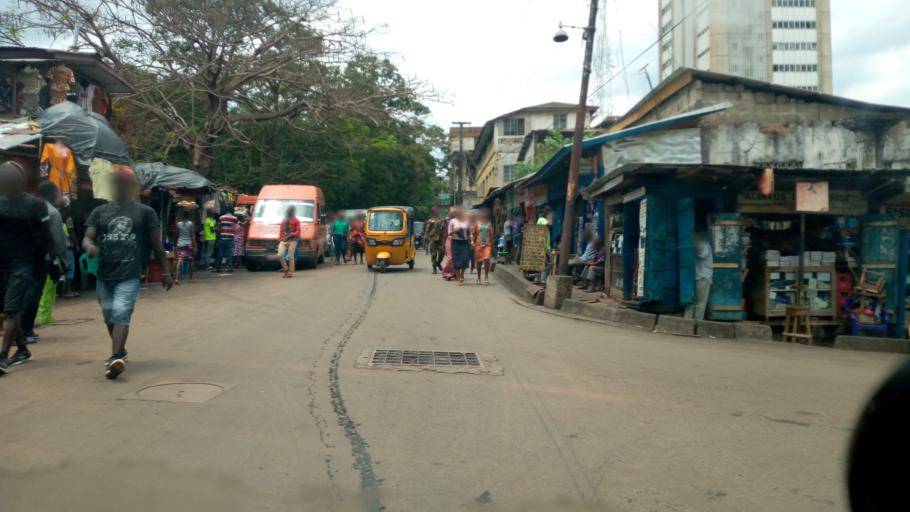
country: SL
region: Western Area
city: Freetown
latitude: 8.4879
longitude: -13.2323
